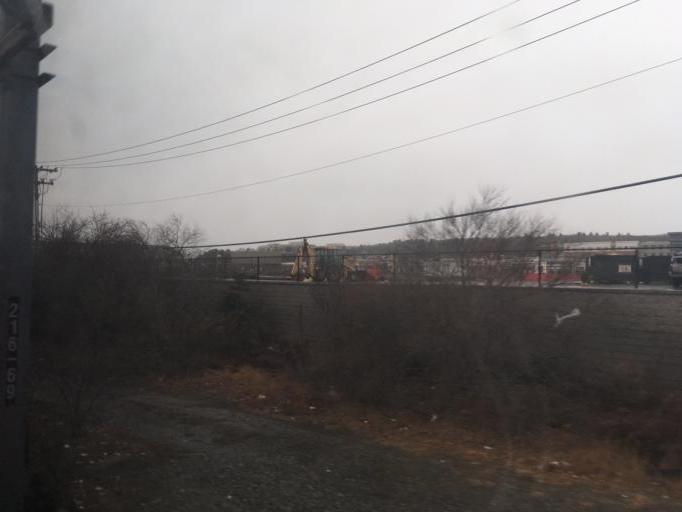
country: US
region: Massachusetts
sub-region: Norfolk County
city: Dedham
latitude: 42.2083
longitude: -71.1482
